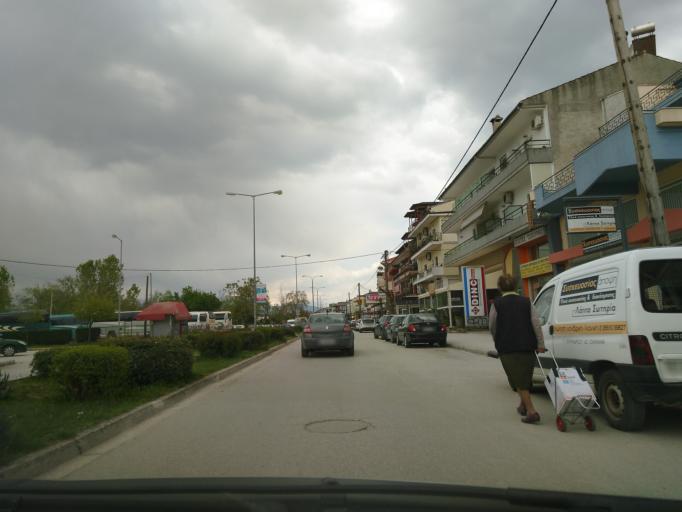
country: GR
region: Epirus
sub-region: Nomos Ioanninon
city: Ioannina
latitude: 39.6741
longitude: 20.8472
